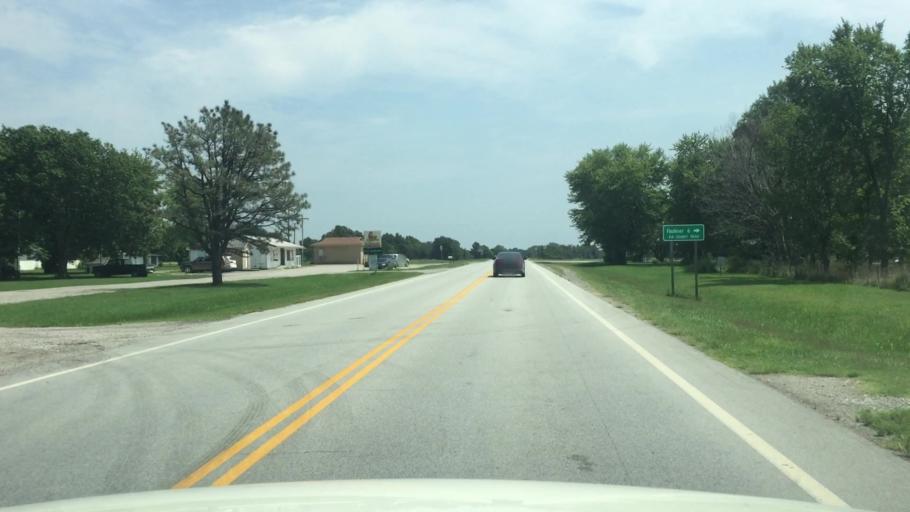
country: US
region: Kansas
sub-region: Labette County
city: Oswego
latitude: 37.1772
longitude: -94.9973
